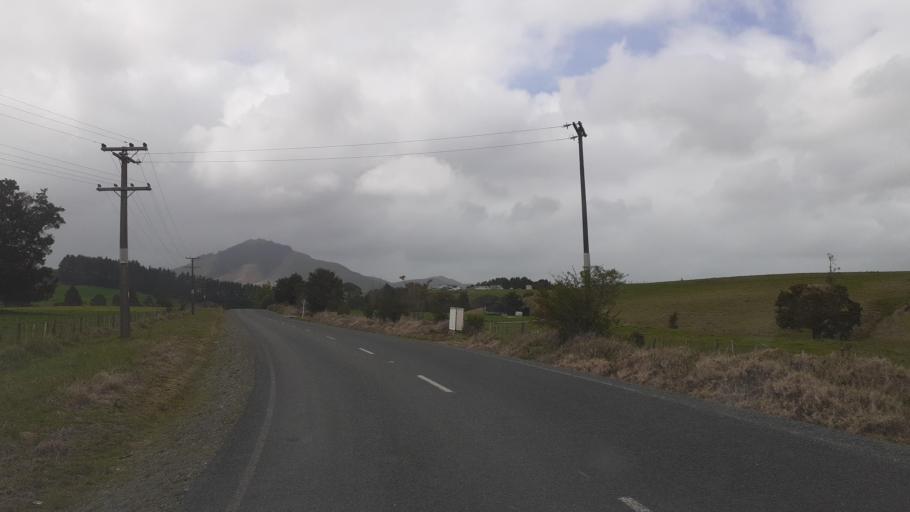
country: NZ
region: Northland
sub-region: Far North District
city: Moerewa
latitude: -35.5915
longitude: 173.9785
